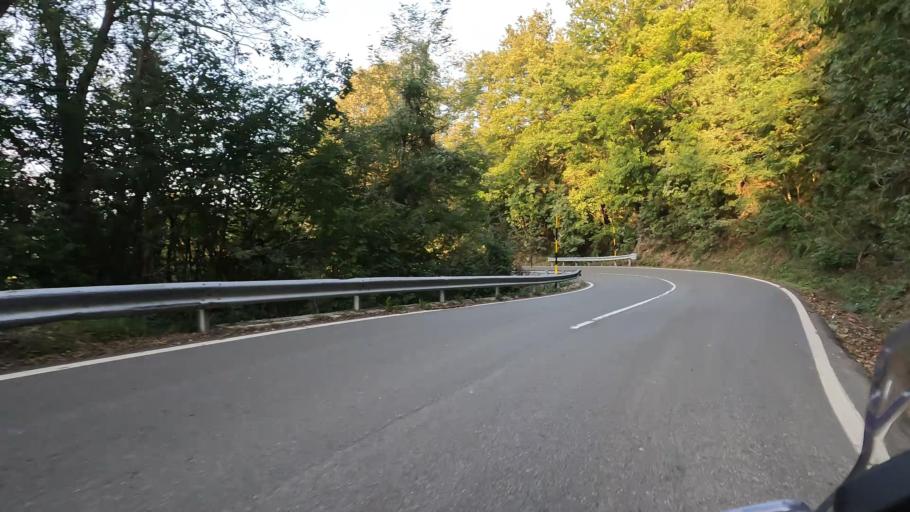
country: IT
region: Liguria
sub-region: Provincia di Savona
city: Sassello
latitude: 44.4879
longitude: 8.4972
